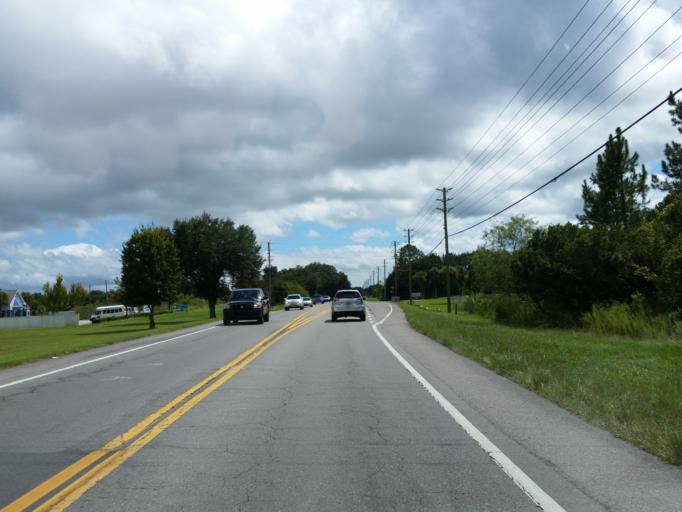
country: US
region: Florida
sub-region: Pasco County
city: Wesley Chapel
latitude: 28.2274
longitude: -82.2867
